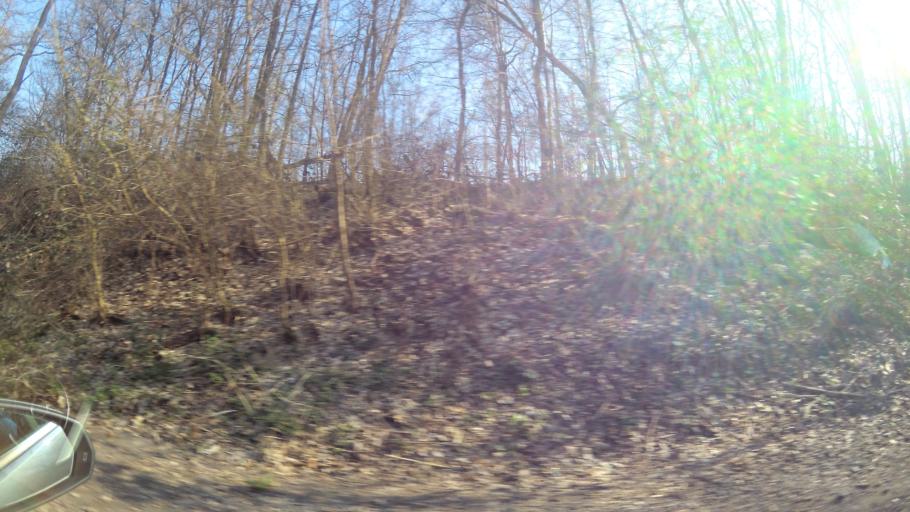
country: DE
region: Saarland
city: Saarbrucken
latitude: 49.2599
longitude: 6.9978
